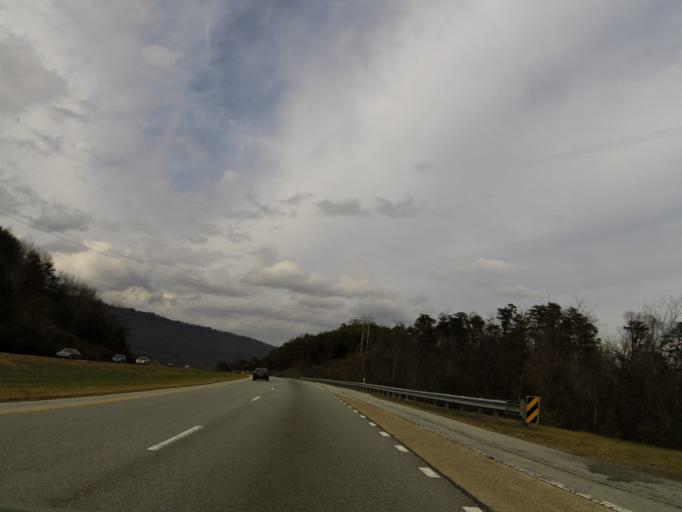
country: US
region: Tennessee
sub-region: Hamilton County
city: Red Bank
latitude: 35.1297
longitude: -85.2929
